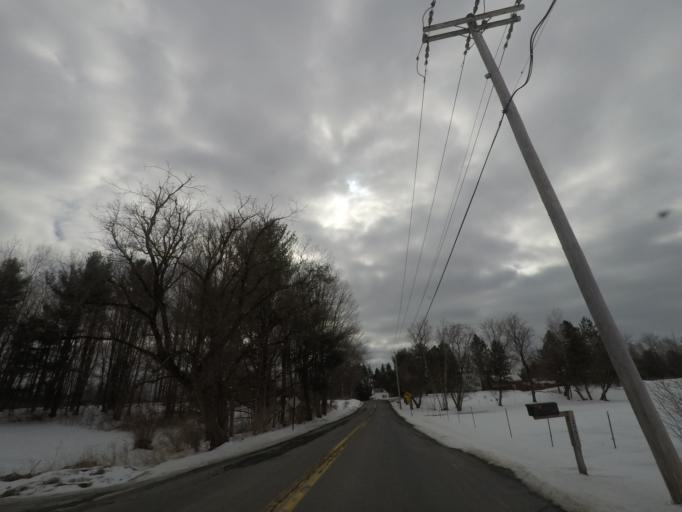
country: US
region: New York
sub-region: Rensselaer County
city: Hoosick Falls
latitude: 42.9477
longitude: -73.4342
